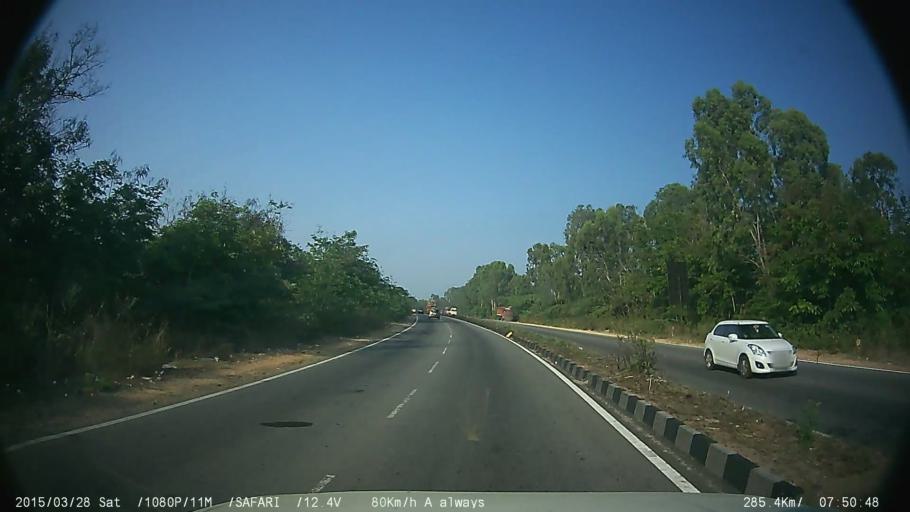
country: IN
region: Karnataka
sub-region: Mandya
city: Shrirangapattana
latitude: 12.4651
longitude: 76.7491
